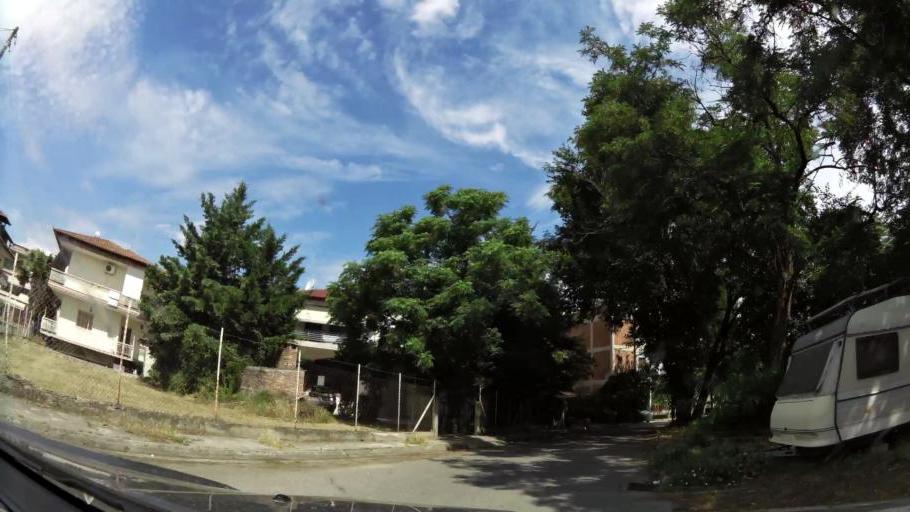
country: GR
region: Central Macedonia
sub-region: Nomos Pierias
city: Katerini
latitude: 40.2663
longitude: 22.4974
